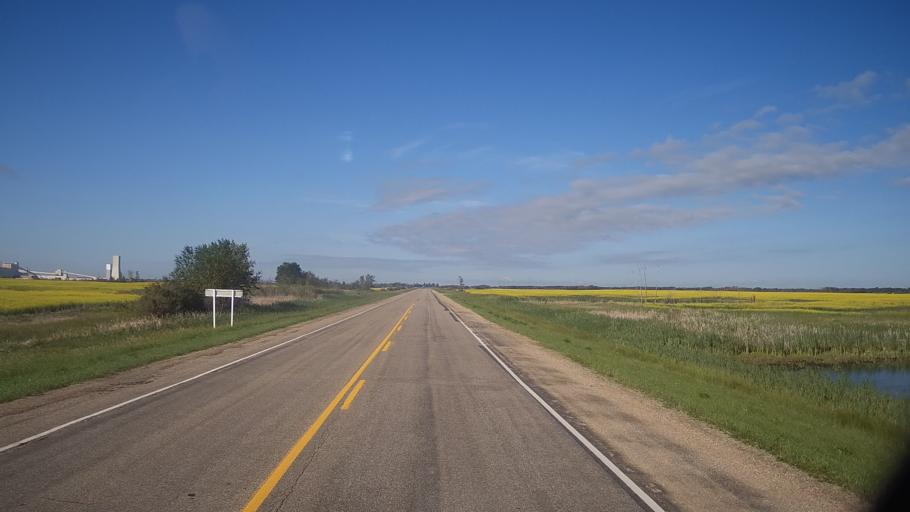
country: CA
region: Saskatchewan
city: Lanigan
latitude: 51.8730
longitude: -105.1961
